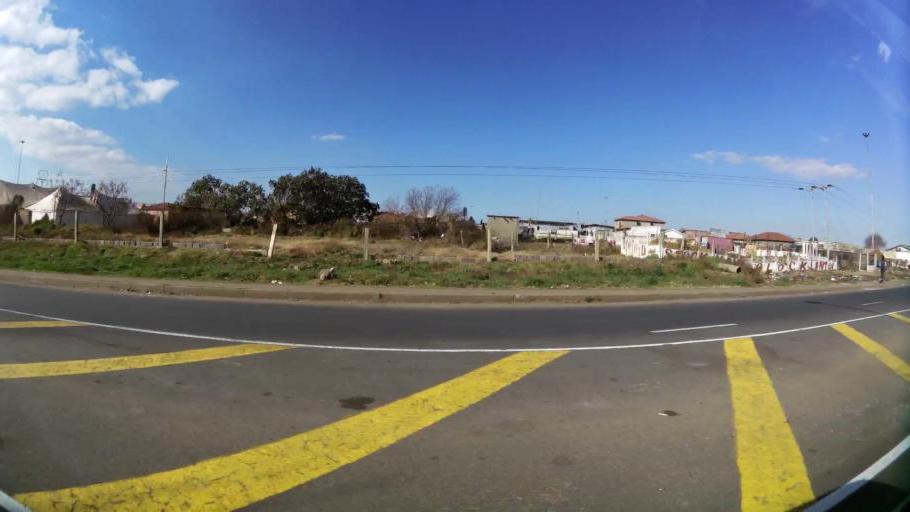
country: ZA
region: Gauteng
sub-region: City of Johannesburg Metropolitan Municipality
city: Soweto
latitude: -26.2731
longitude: 27.8907
